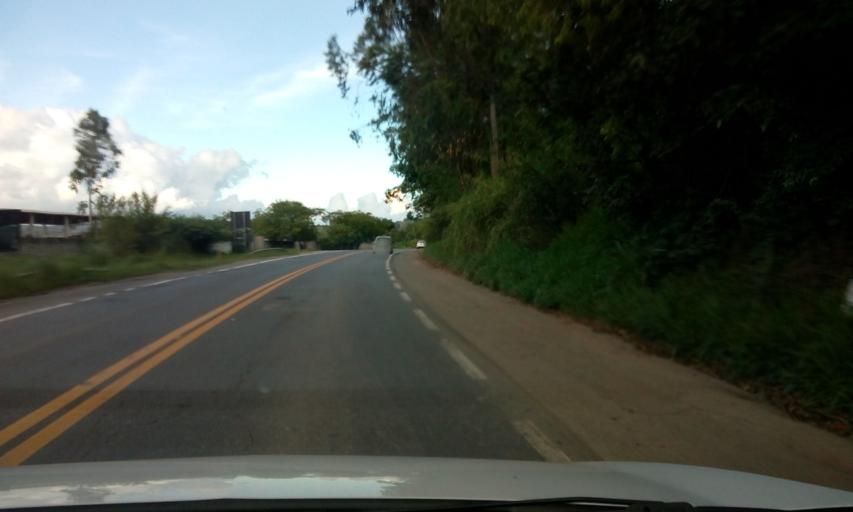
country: BR
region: Sao Paulo
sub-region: Itatiba
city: Itatiba
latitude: -22.9958
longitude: -46.8045
